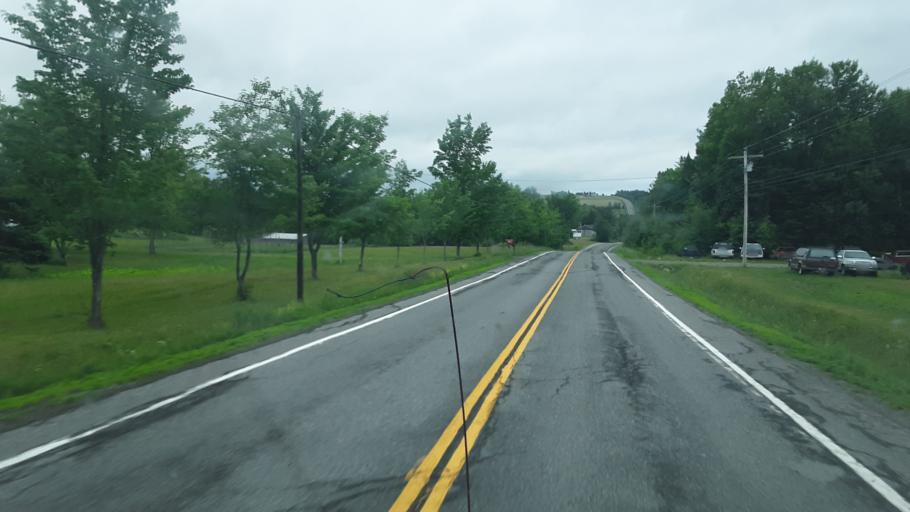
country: US
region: Maine
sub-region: Penobscot County
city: Patten
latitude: 46.0618
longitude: -68.4391
